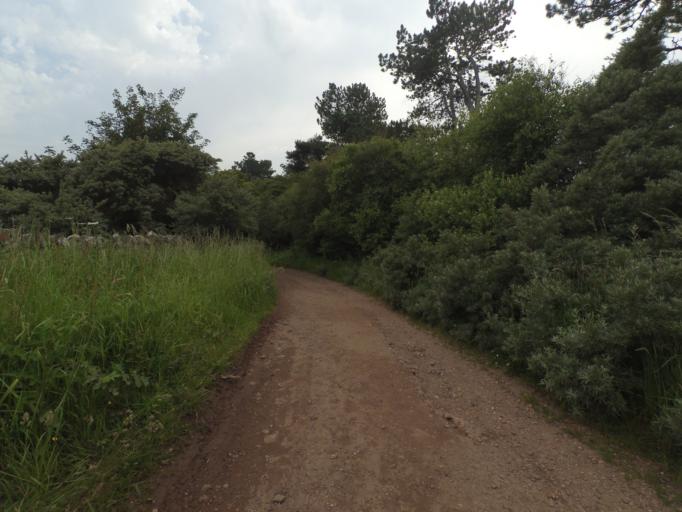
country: GB
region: Scotland
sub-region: East Lothian
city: East Linton
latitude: 56.0252
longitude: -2.6021
